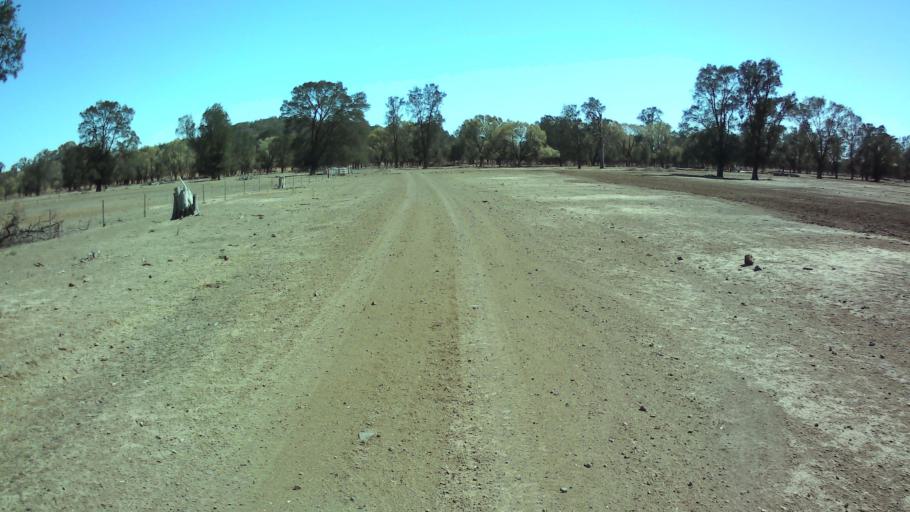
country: AU
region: New South Wales
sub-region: Bland
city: West Wyalong
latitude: -33.7411
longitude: 147.6618
